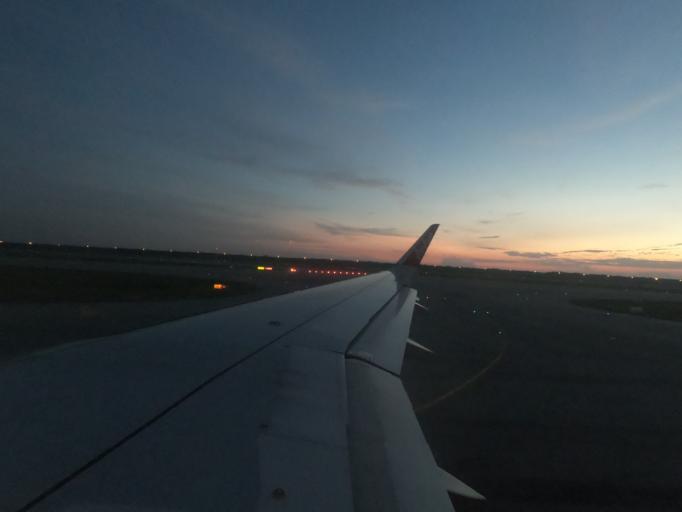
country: MY
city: Sungai Pelek New Village
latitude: 2.7278
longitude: 101.6878
